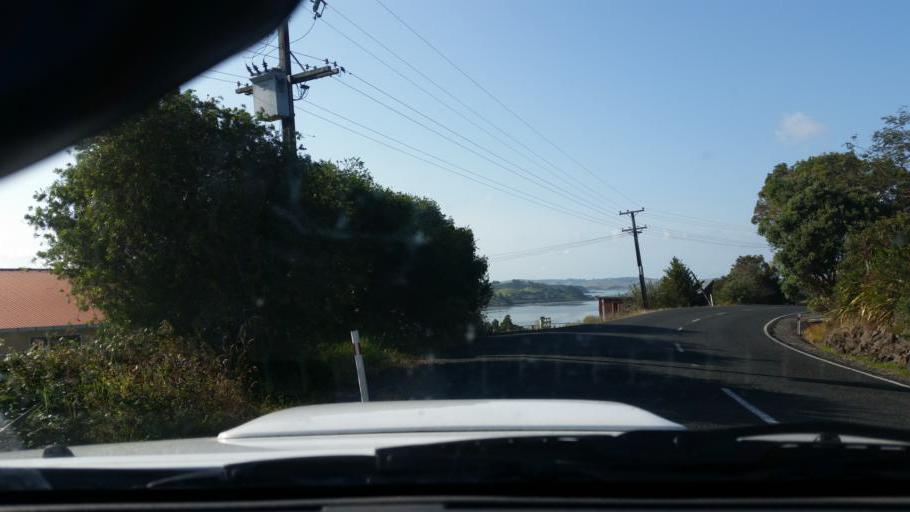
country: NZ
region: Northland
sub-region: Whangarei
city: Ruakaka
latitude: -36.1293
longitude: 174.2301
